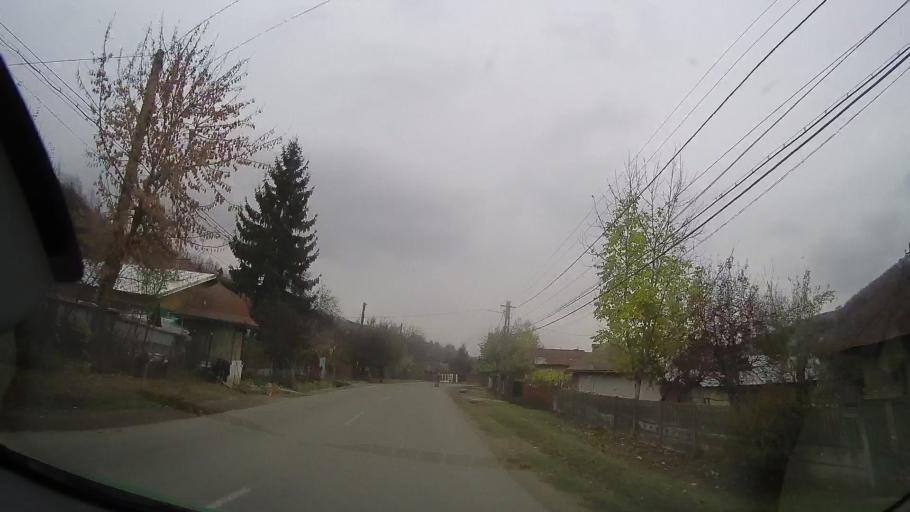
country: RO
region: Prahova
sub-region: Comuna Ceptura
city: Ceptura de Jos
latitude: 45.0349
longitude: 26.3184
